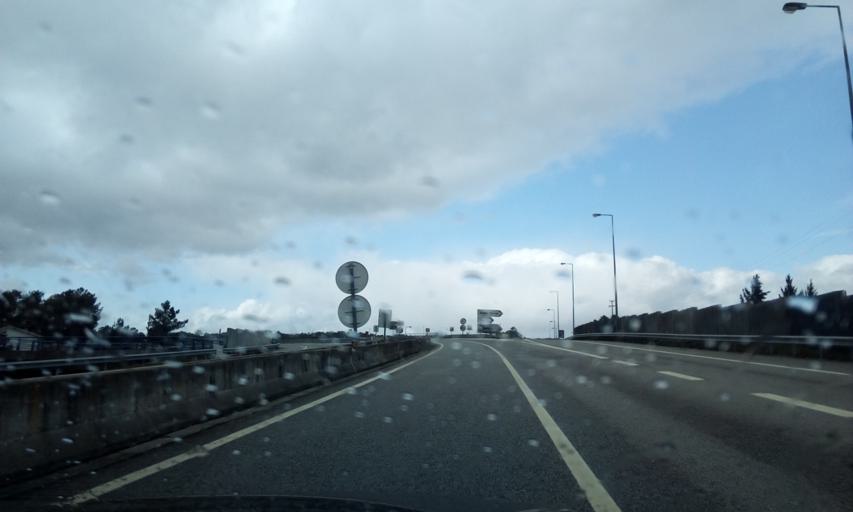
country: PT
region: Viseu
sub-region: Viseu
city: Rio de Loba
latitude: 40.6520
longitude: -7.8614
